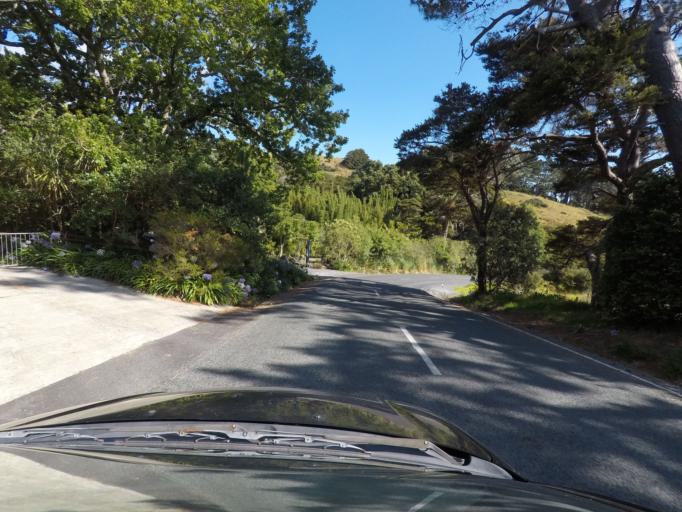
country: NZ
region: Auckland
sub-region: Auckland
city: Warkworth
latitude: -36.2783
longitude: 174.7906
